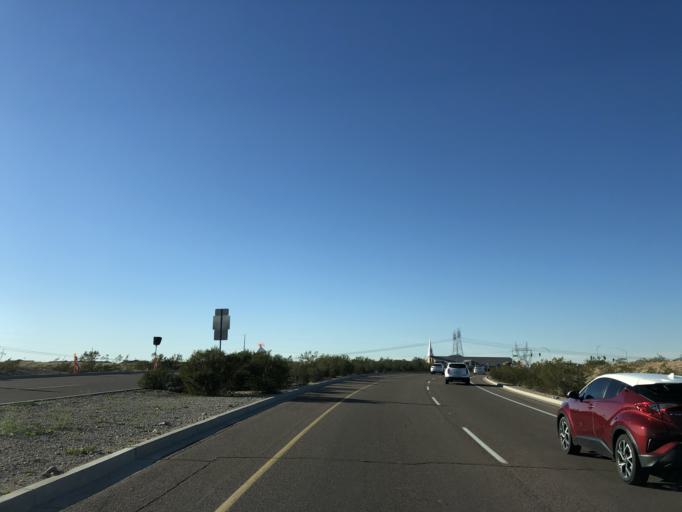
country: US
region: Arizona
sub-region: Maricopa County
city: Sun City West
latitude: 33.7138
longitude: -112.3138
